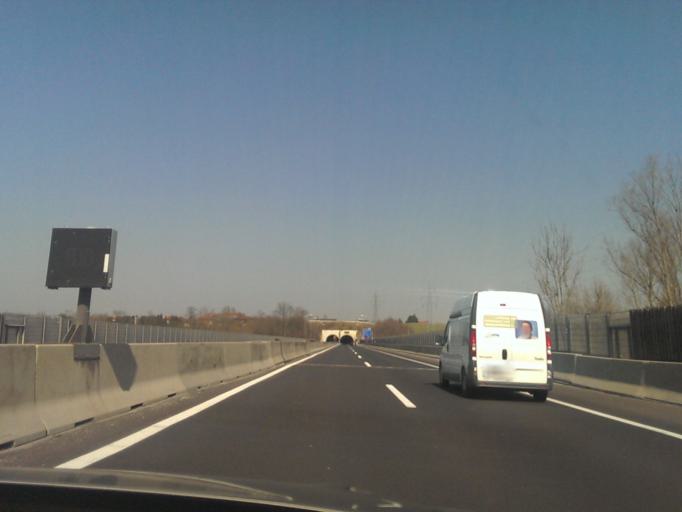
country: AT
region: Upper Austria
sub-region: Politischer Bezirk Kirchdorf an der Krems
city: Micheldorf in Oberoesterreich
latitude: 47.9154
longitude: 14.1014
